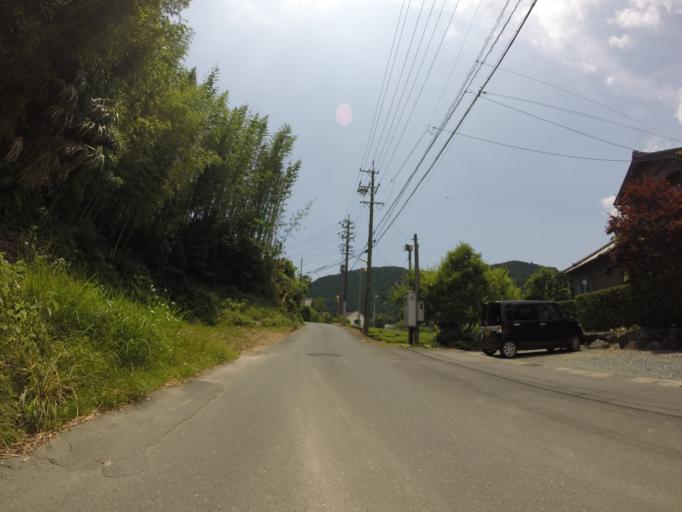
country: JP
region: Shizuoka
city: Kanaya
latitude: 34.8055
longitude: 138.0728
